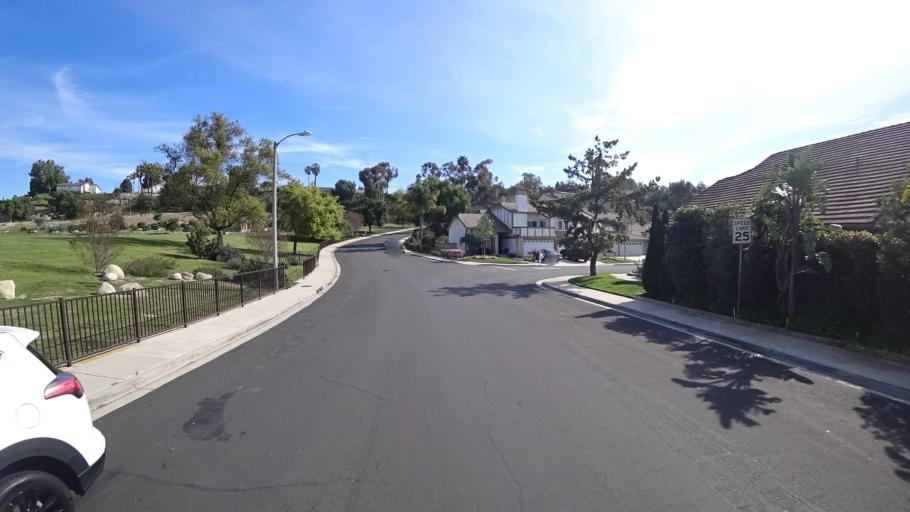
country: US
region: California
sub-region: Ventura County
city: Thousand Oaks
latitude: 34.2243
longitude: -118.8421
